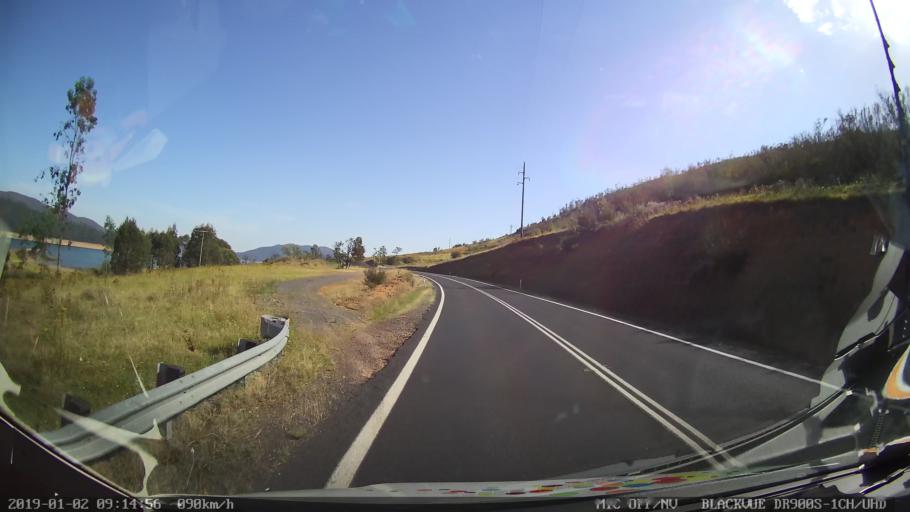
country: AU
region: New South Wales
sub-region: Tumut Shire
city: Tumut
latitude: -35.4714
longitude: 148.2786
